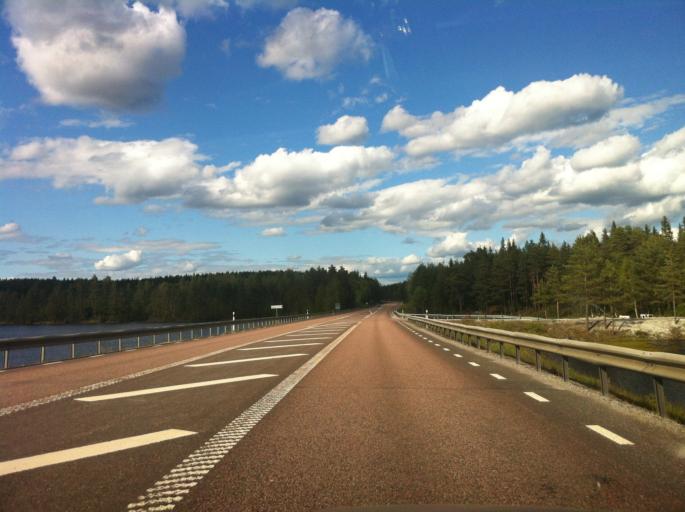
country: SE
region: Vaermland
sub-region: Filipstads Kommun
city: Filipstad
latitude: 59.7220
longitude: 14.2092
